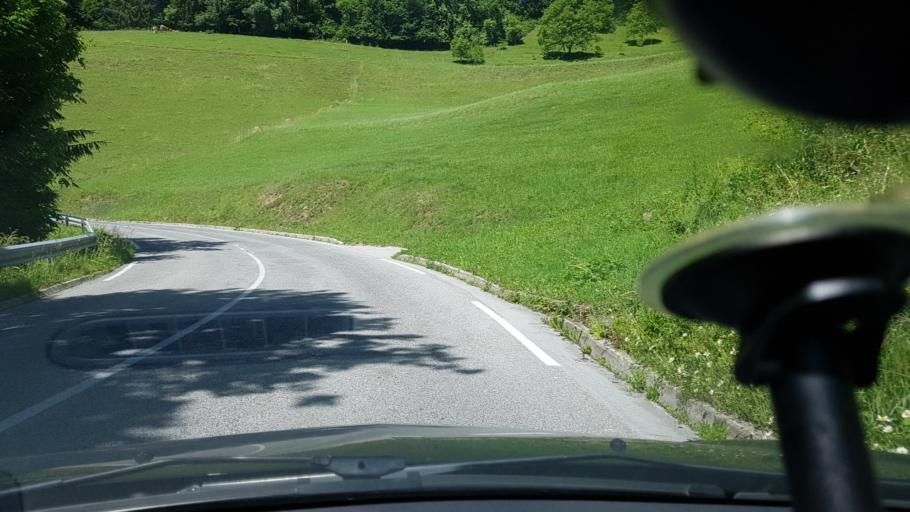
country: SI
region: Zrece
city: Zrece
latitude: 46.3968
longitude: 15.3752
